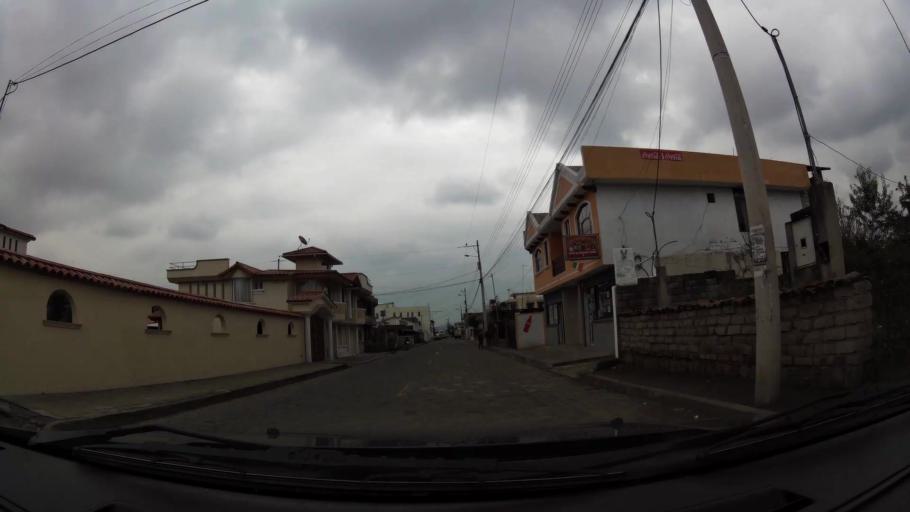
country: EC
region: Pichincha
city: Sangolqui
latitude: -0.3371
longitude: -78.4719
